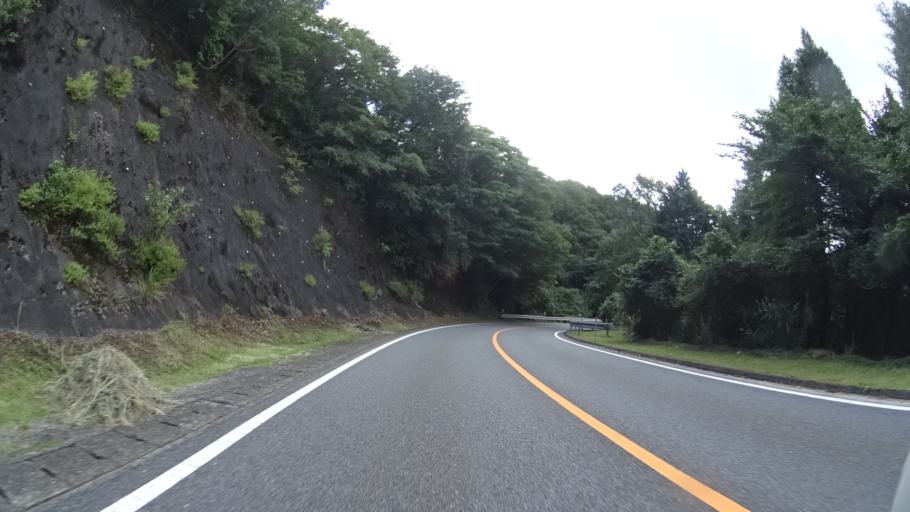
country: JP
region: Oita
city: Tsukawaki
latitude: 33.2437
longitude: 131.2844
